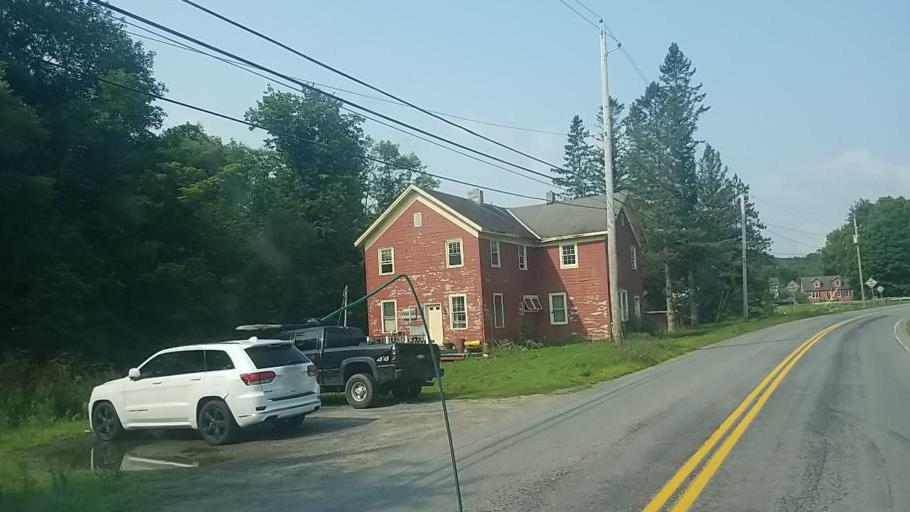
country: US
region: New York
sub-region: Montgomery County
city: Fonda
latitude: 42.9884
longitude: -74.4342
